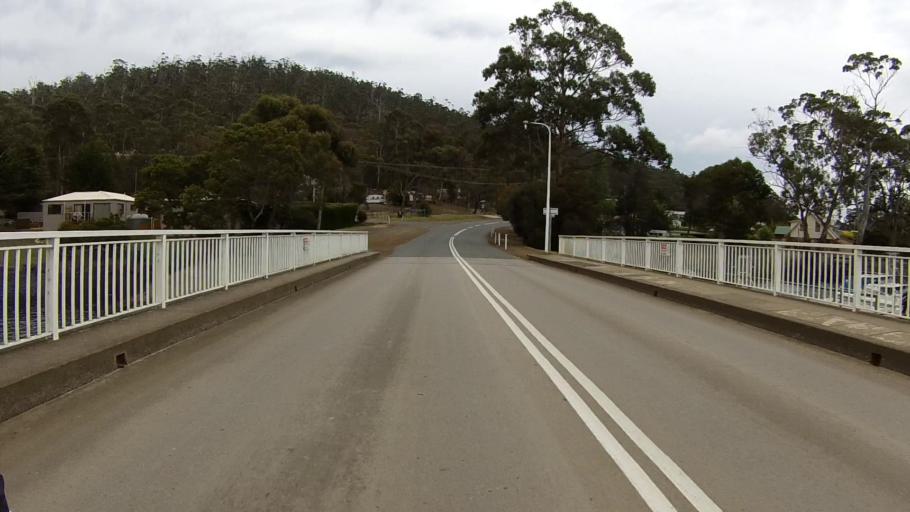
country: AU
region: Tasmania
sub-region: Sorell
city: Sorell
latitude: -42.5573
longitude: 147.8716
